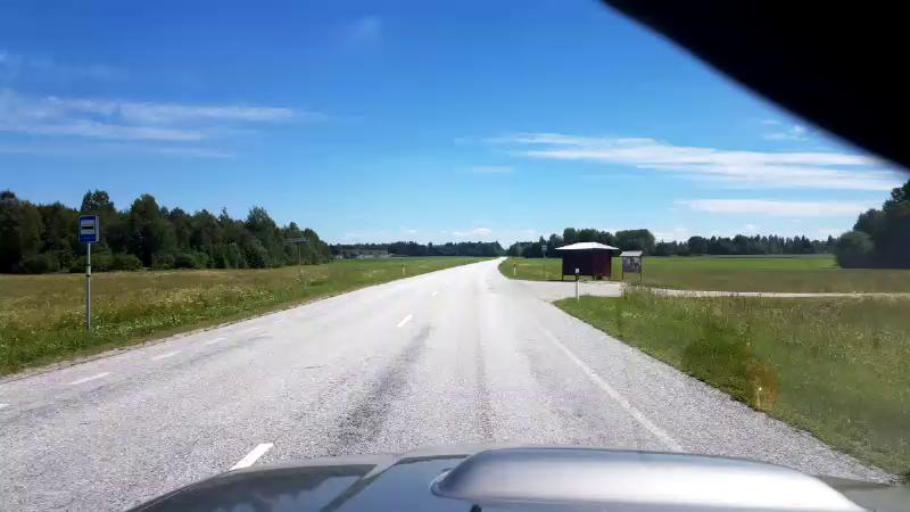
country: EE
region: Laeaene-Virumaa
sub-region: Rakke vald
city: Rakke
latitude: 58.9582
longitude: 26.1677
